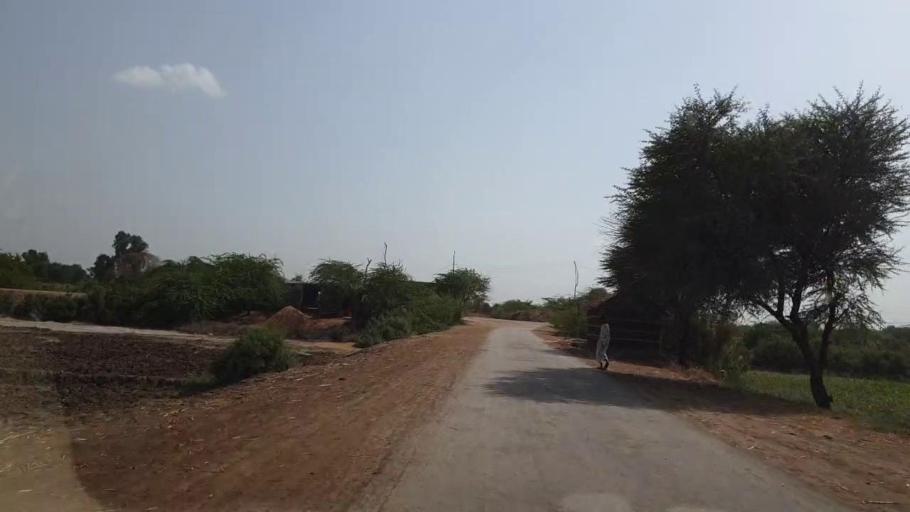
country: PK
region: Sindh
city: Rajo Khanani
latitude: 25.0110
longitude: 68.8726
